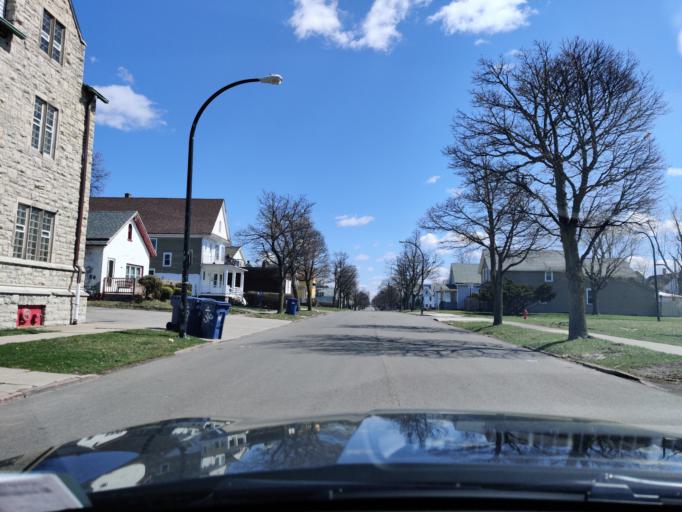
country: US
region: New York
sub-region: Erie County
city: Buffalo
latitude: 42.9194
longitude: -78.8591
